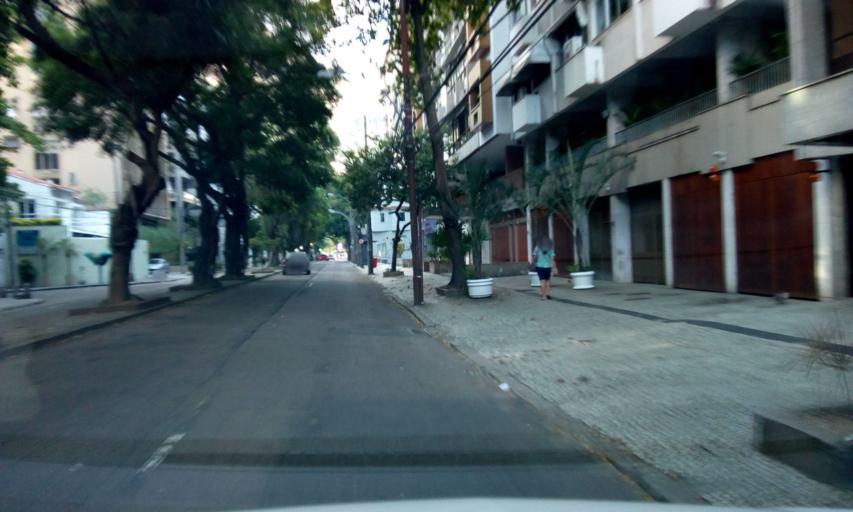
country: BR
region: Rio de Janeiro
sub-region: Rio De Janeiro
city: Rio de Janeiro
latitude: -22.9638
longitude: -43.2028
